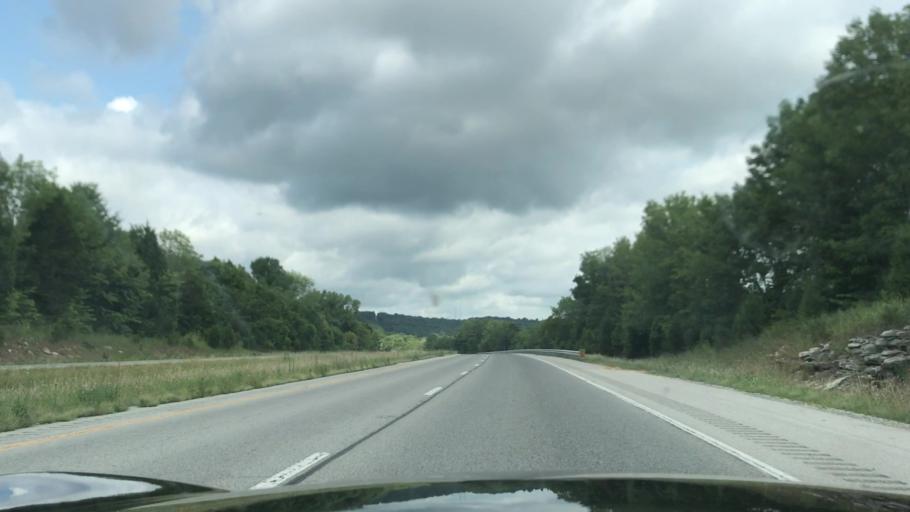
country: US
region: Kentucky
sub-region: Warren County
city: Bowling Green
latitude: 37.0052
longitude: -86.5078
